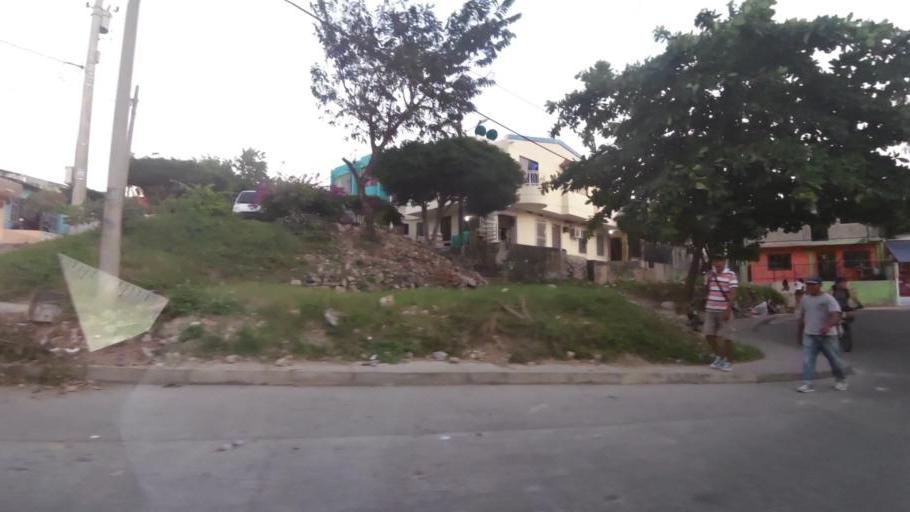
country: CO
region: Bolivar
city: Cartagena
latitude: 10.4030
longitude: -75.5146
